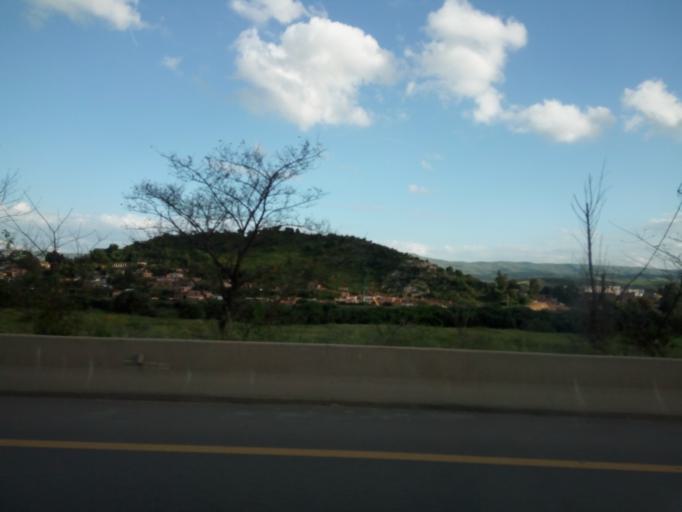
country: DZ
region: Tipaza
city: Hadjout
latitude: 36.3780
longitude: 2.4681
